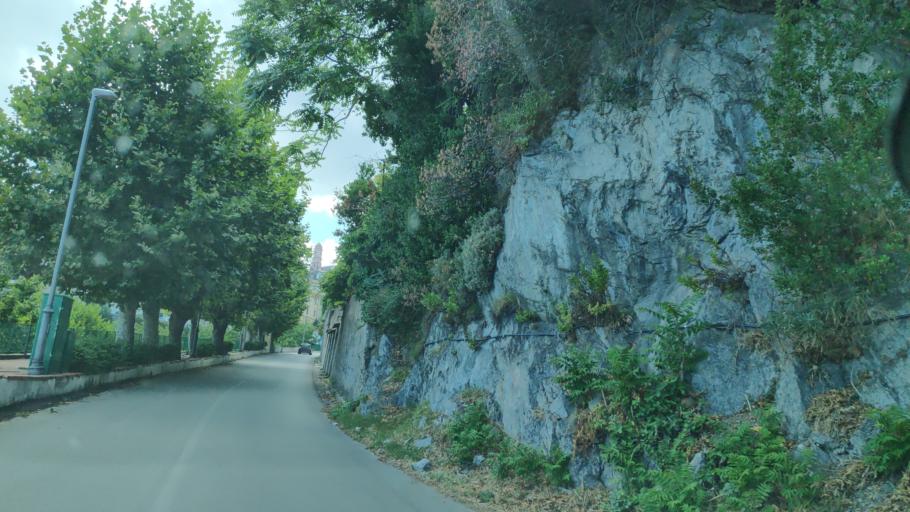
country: IT
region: Campania
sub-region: Provincia di Salerno
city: Vietri sul Mare
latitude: 40.6705
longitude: 14.7322
